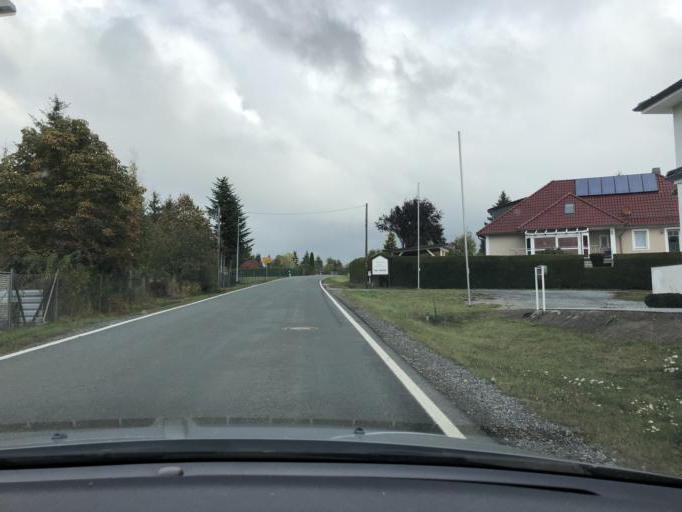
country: DE
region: Thuringia
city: Anrode
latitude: 51.2549
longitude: 10.3503
